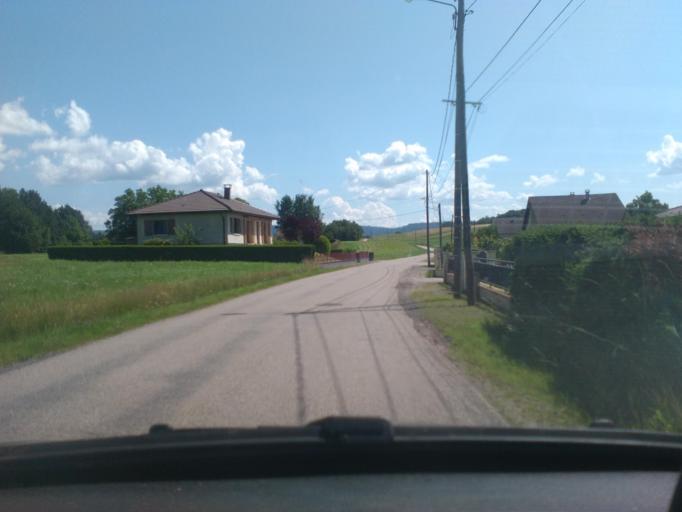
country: FR
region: Lorraine
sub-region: Departement des Vosges
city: Etival-Clairefontaine
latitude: 48.3538
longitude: 6.8653
